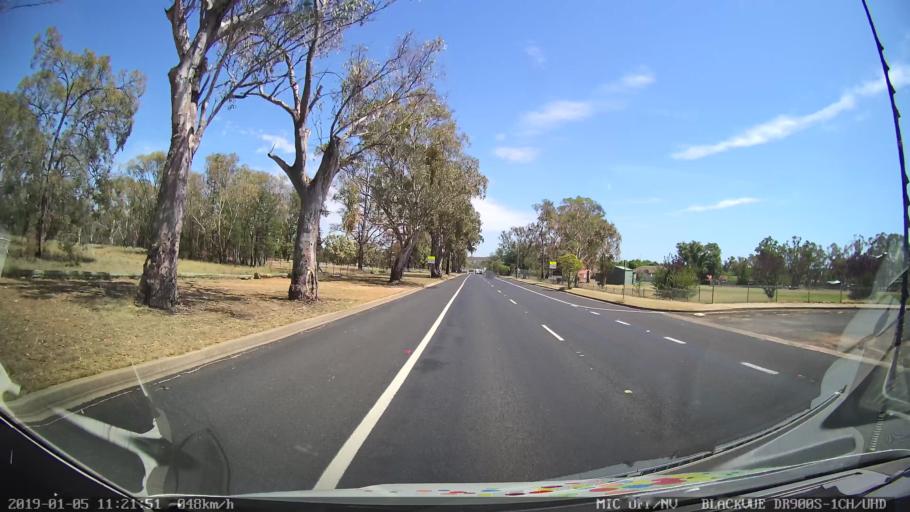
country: AU
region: New South Wales
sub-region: Warrumbungle Shire
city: Coonabarabran
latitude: -31.2822
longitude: 149.2823
